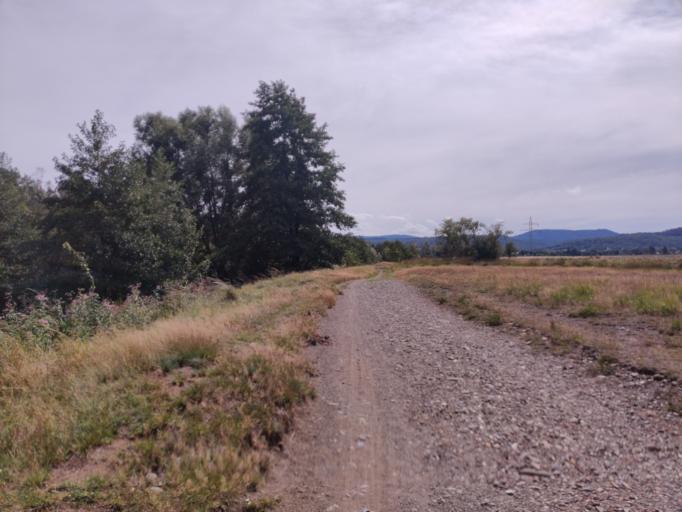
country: DE
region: Lower Saxony
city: Langelsheim
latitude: 51.9532
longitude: 10.3484
